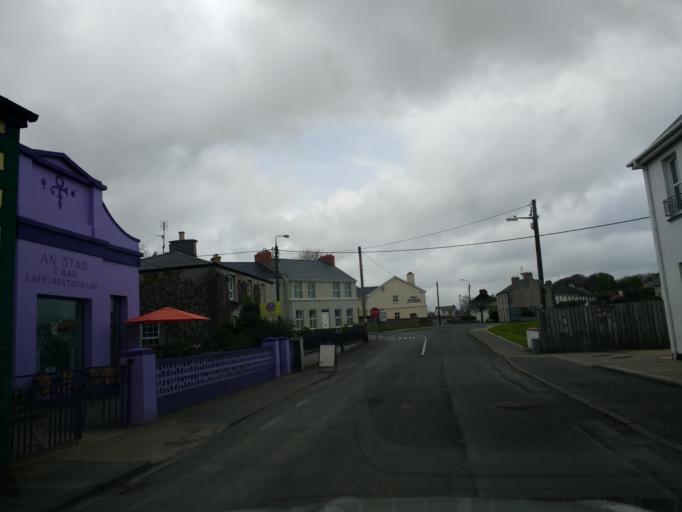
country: IE
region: Ulster
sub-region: County Donegal
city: Buncrana
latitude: 55.0946
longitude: -7.5372
